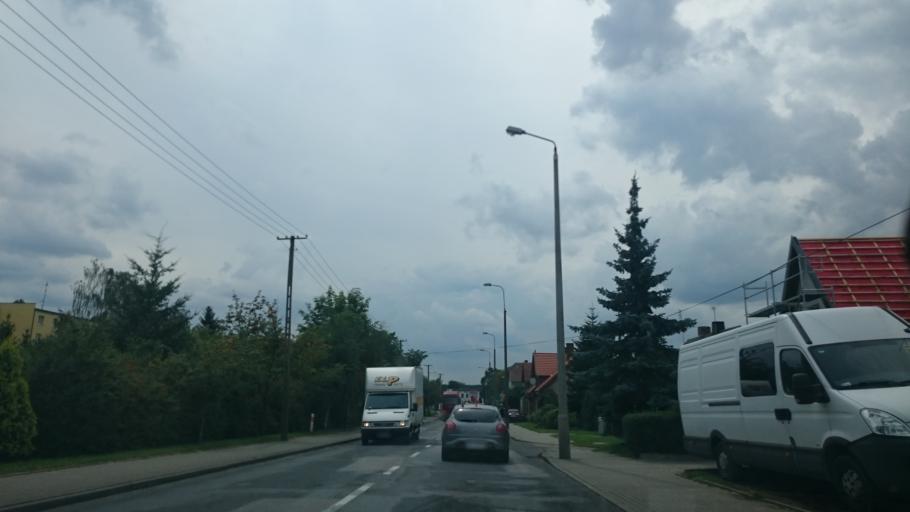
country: PL
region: Kujawsko-Pomorskie
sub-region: Powiat tucholski
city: Tuchola
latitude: 53.5827
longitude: 17.8729
